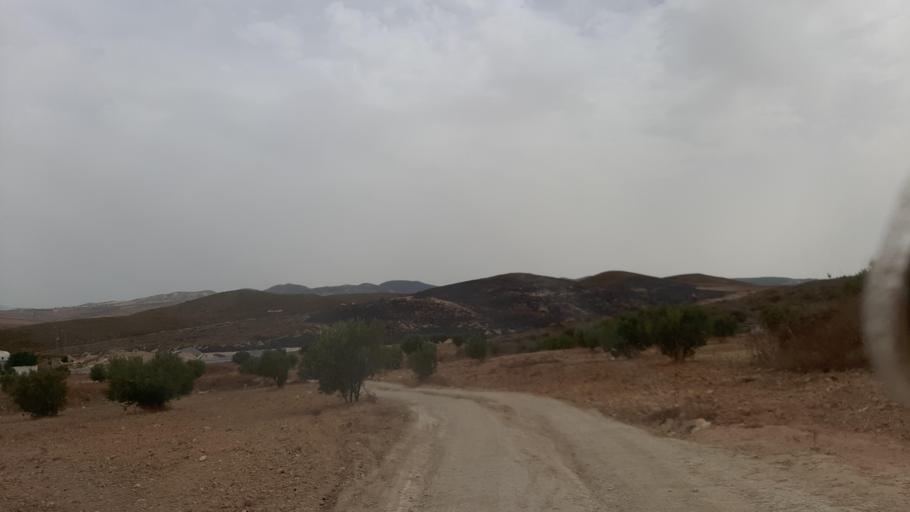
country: TN
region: Tunis
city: La Mohammedia
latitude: 36.5653
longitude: 10.1485
